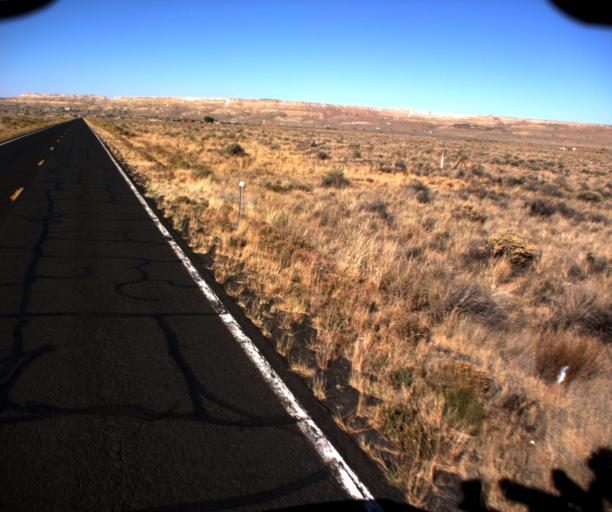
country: US
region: Arizona
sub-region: Navajo County
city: First Mesa
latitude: 35.8416
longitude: -110.3317
